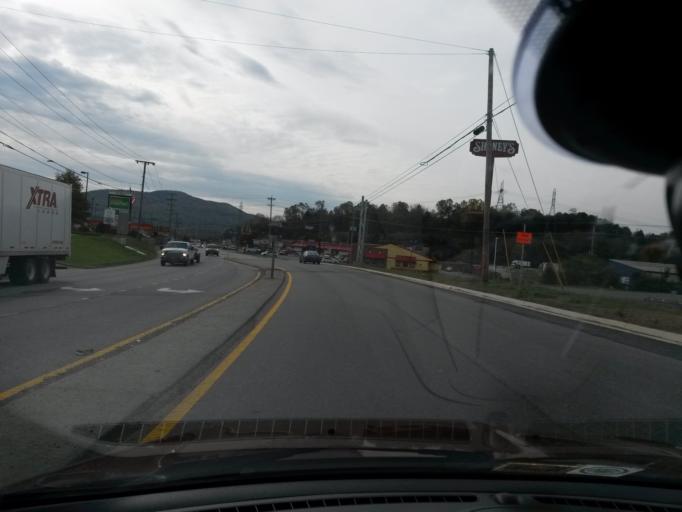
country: US
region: Virginia
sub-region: Botetourt County
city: Cloverdale
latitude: 37.3866
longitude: -79.9030
